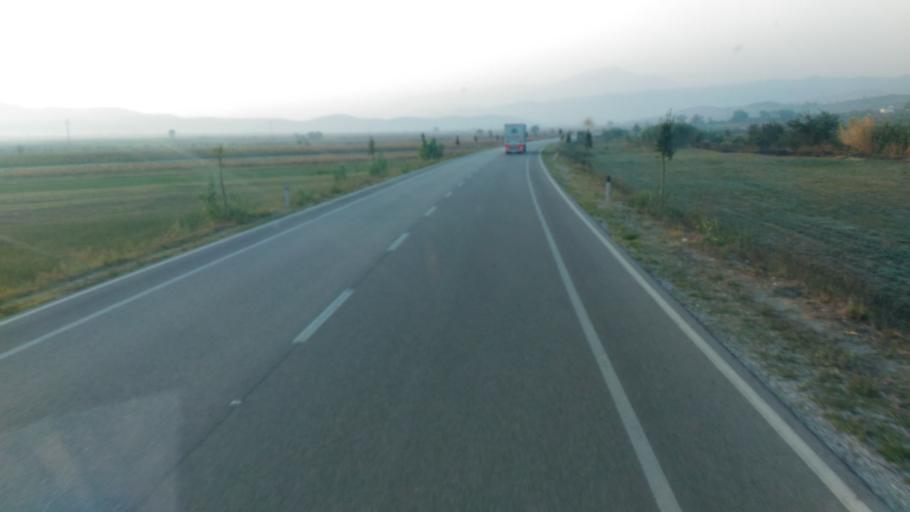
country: AL
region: Fier
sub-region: Rrethi i Fierit
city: Cakran
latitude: 40.5832
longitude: 19.6183
